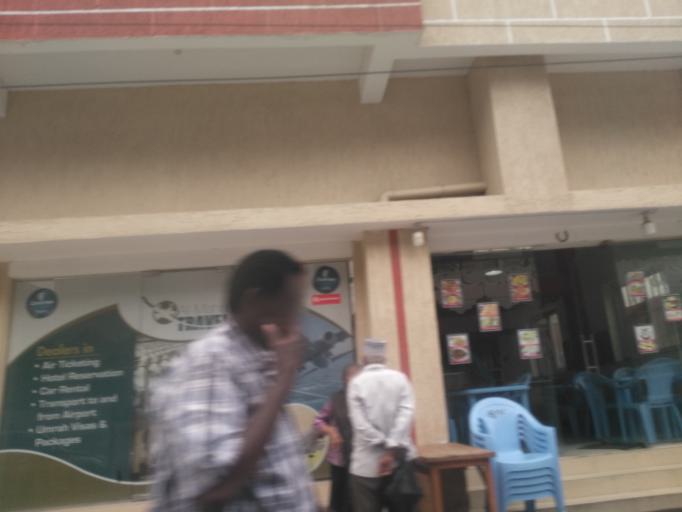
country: TZ
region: Dar es Salaam
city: Dar es Salaam
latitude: -6.8173
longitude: 39.2778
